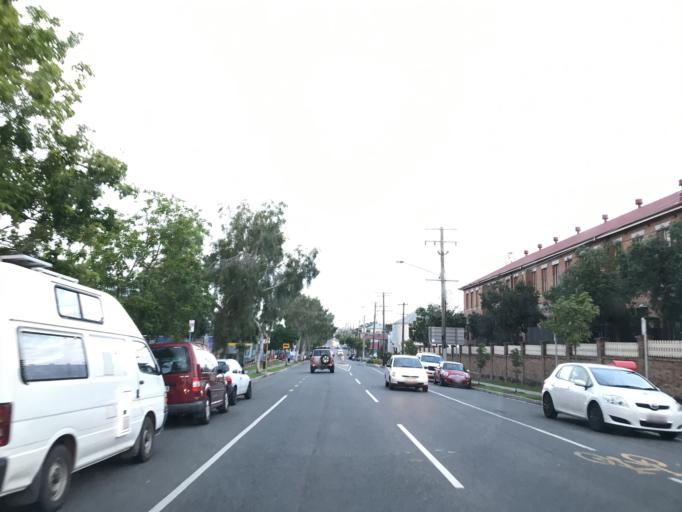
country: AU
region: Queensland
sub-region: Brisbane
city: Toowong
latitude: -27.4866
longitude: 153.0012
